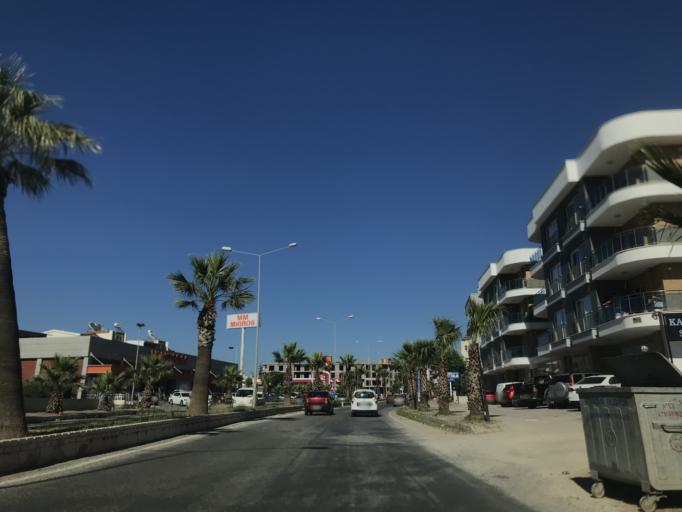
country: TR
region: Aydin
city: Davutlar
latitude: 37.7335
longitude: 27.2819
